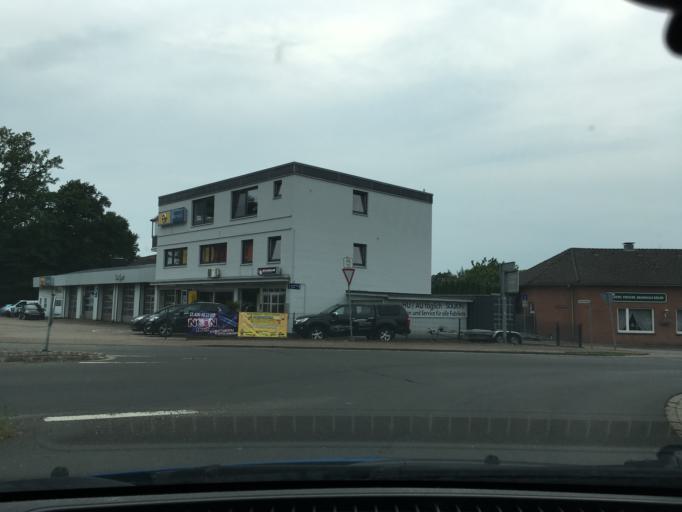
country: DE
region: Lower Saxony
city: Tostedt
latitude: 53.2832
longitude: 9.7159
